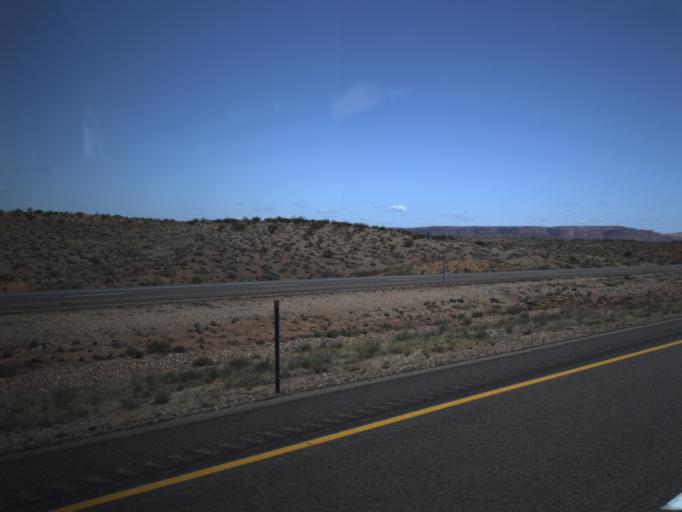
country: US
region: Utah
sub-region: Washington County
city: Saint George
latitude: 37.0006
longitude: -113.5536
